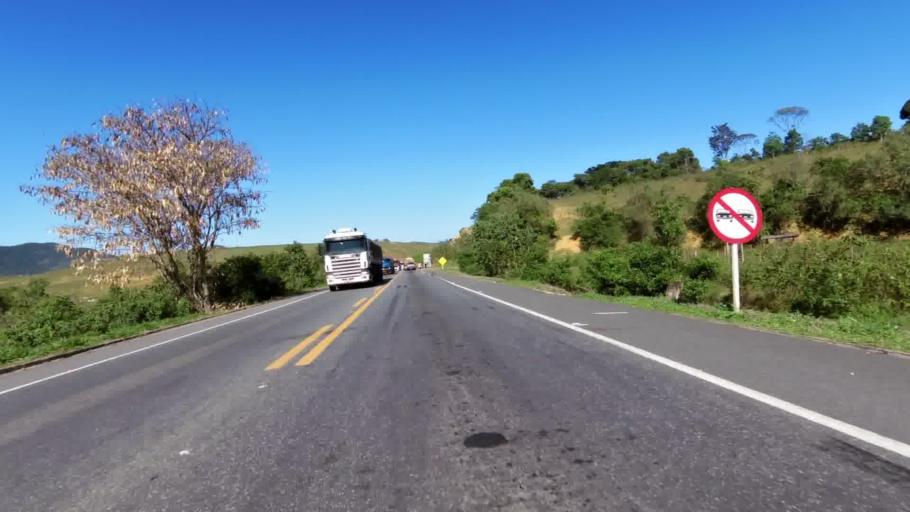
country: BR
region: Espirito Santo
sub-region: Alfredo Chaves
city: Alfredo Chaves
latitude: -20.7152
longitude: -40.7284
